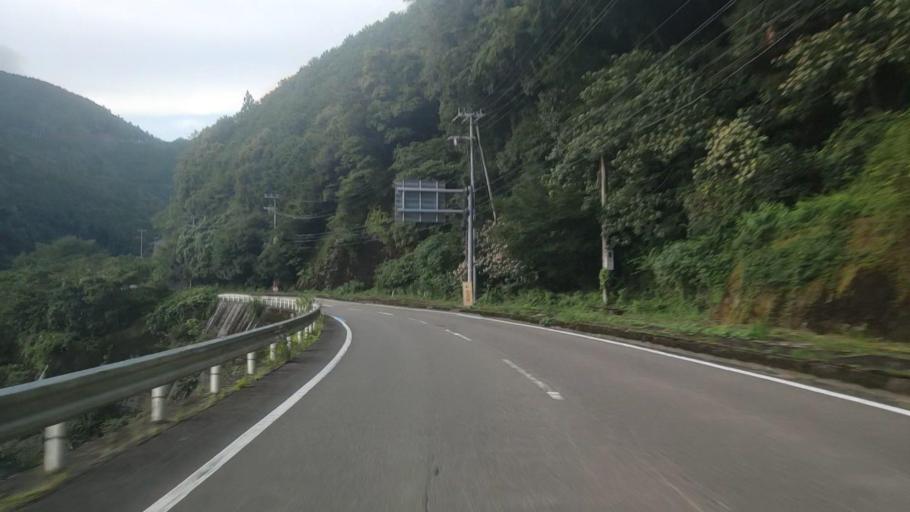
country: JP
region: Wakayama
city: Shingu
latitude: 33.8180
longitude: 135.7675
